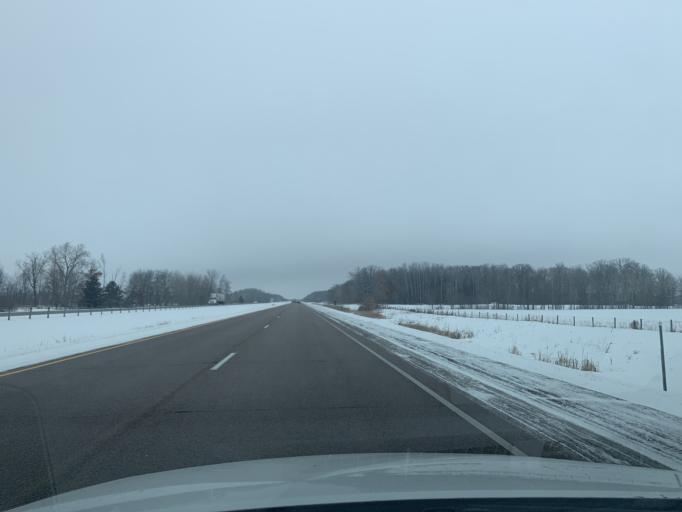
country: US
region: Minnesota
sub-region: Chisago County
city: Rush City
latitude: 45.6499
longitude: -92.9922
